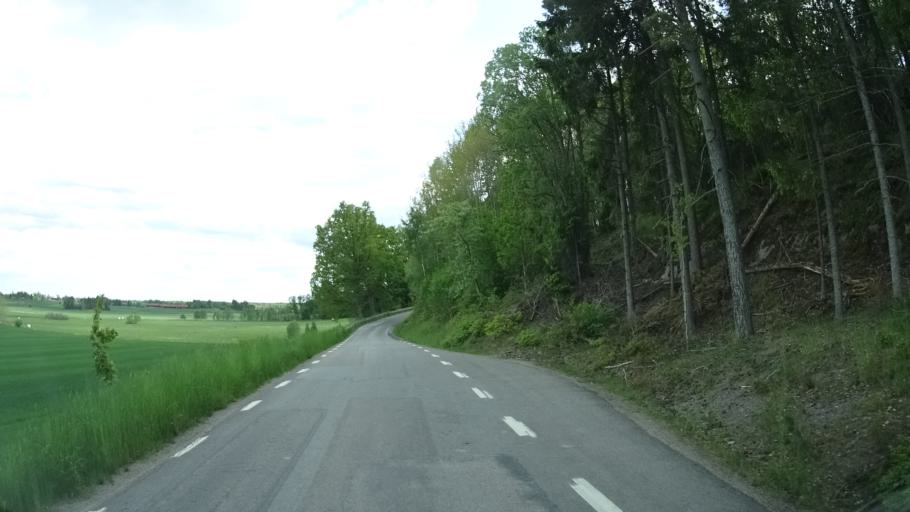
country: SE
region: OEstergoetland
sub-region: Finspangs Kommun
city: Finspang
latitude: 58.5925
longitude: 15.7750
